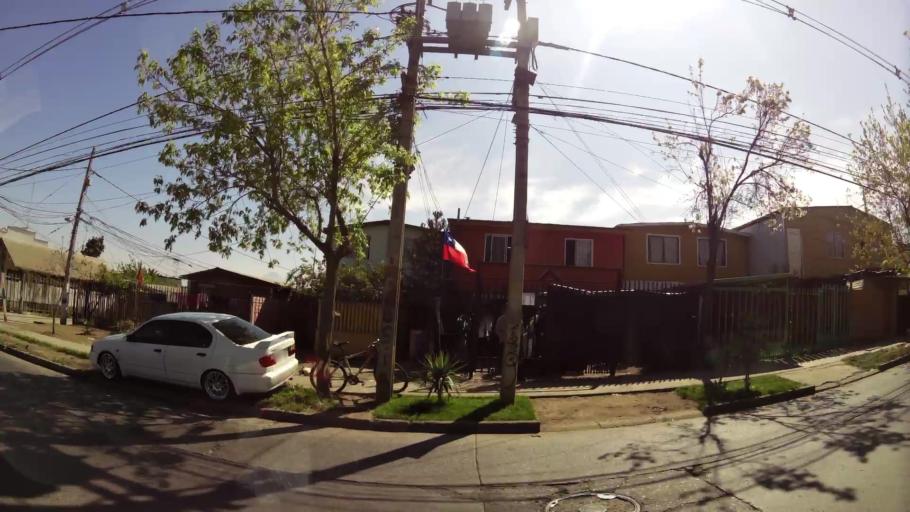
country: CL
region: Santiago Metropolitan
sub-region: Provincia de Santiago
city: Villa Presidente Frei, Nunoa, Santiago, Chile
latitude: -33.4589
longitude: -70.5349
